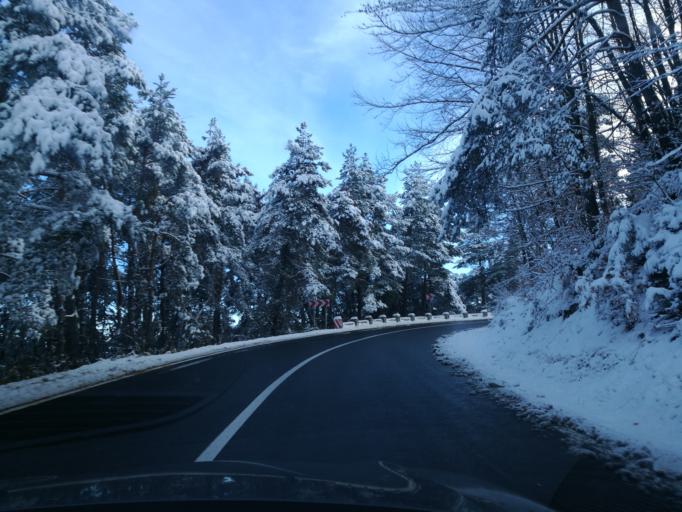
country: RO
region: Brasov
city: Brasov
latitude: 45.6331
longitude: 25.5611
